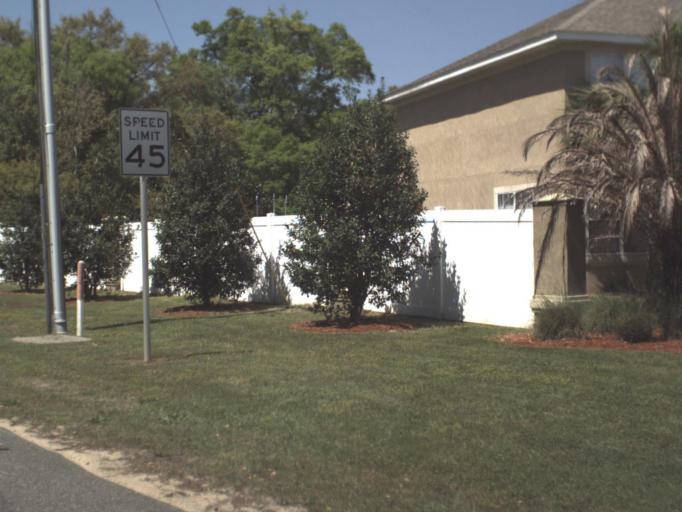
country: US
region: Florida
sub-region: Escambia County
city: Bellview
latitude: 30.4844
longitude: -87.3140
